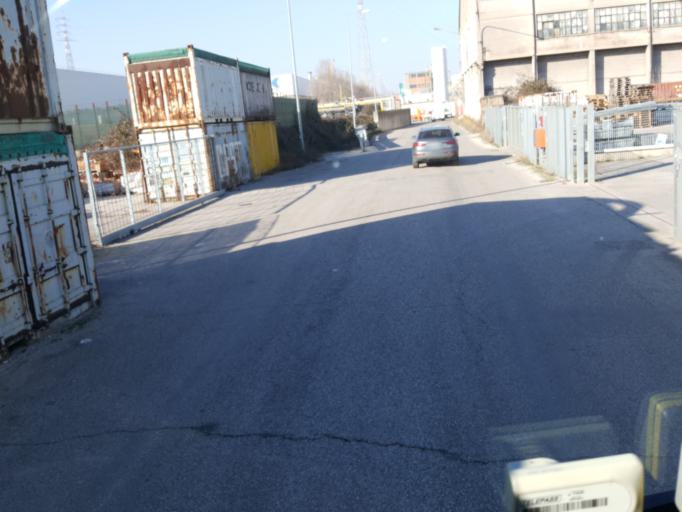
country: IT
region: Veneto
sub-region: Provincia di Venezia
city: Mestre
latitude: 45.4602
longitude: 12.2413
